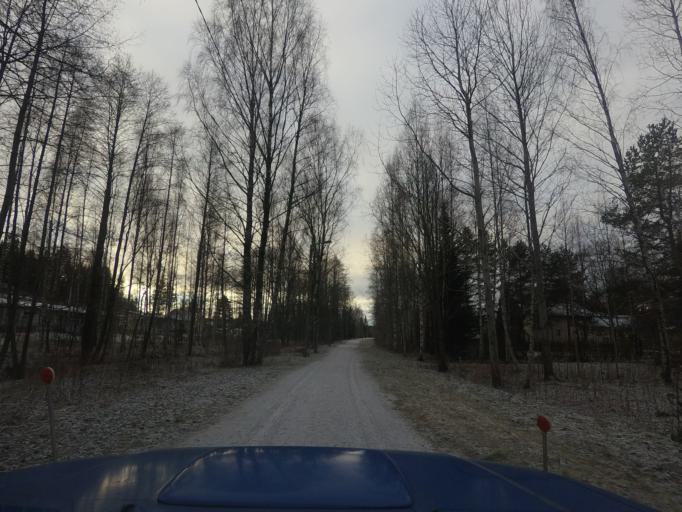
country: FI
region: Uusimaa
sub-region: Helsinki
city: Espoo
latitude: 60.1939
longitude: 24.6574
